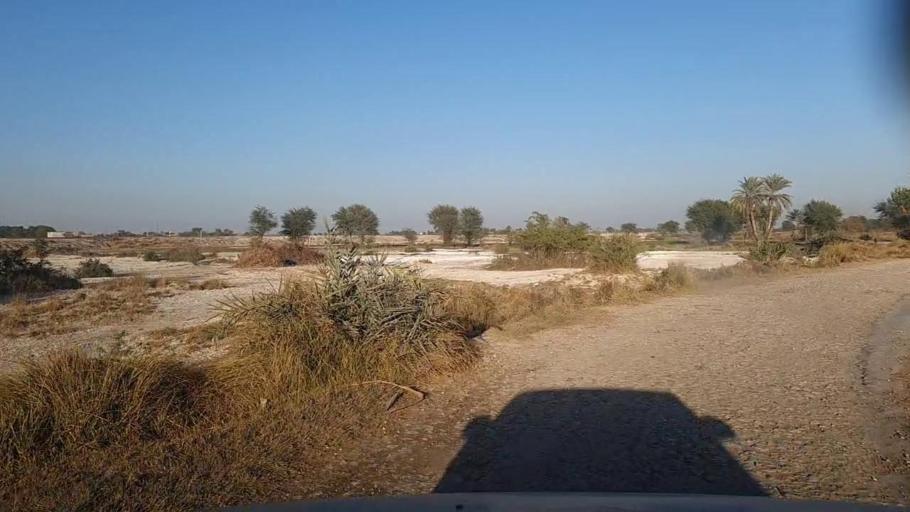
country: PK
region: Sindh
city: Khairpur
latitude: 28.0415
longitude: 69.7290
